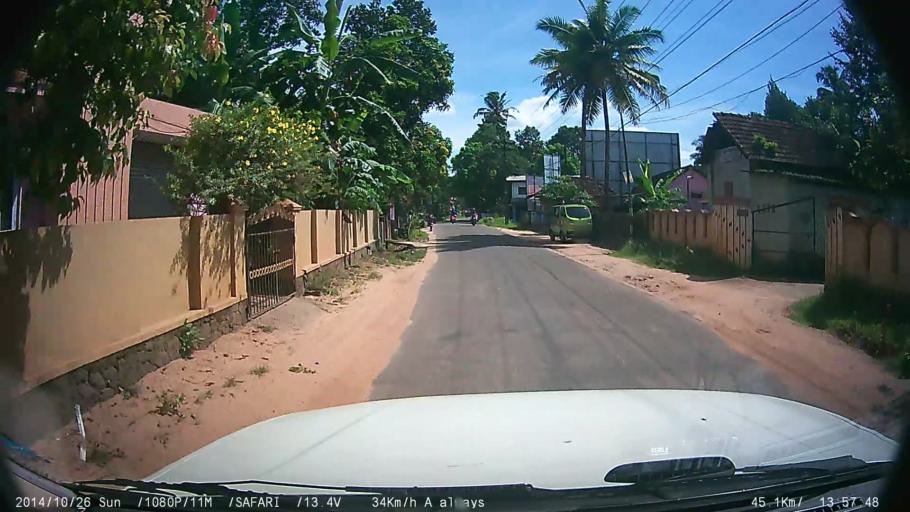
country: IN
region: Kerala
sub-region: Kottayam
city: Changanacheri
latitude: 9.4371
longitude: 76.5612
